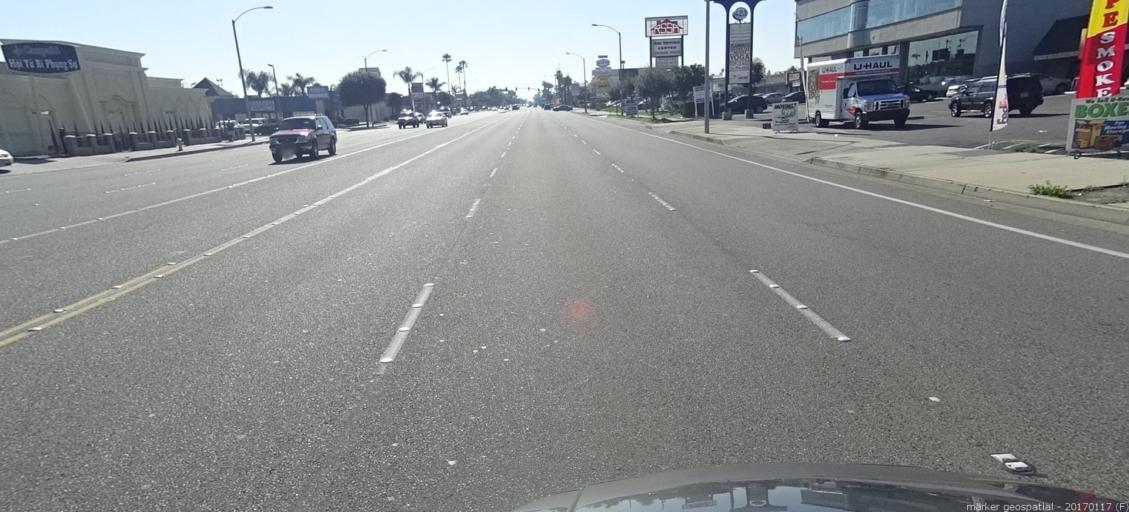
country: US
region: California
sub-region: Orange County
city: Stanton
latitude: 33.8274
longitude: -117.9590
